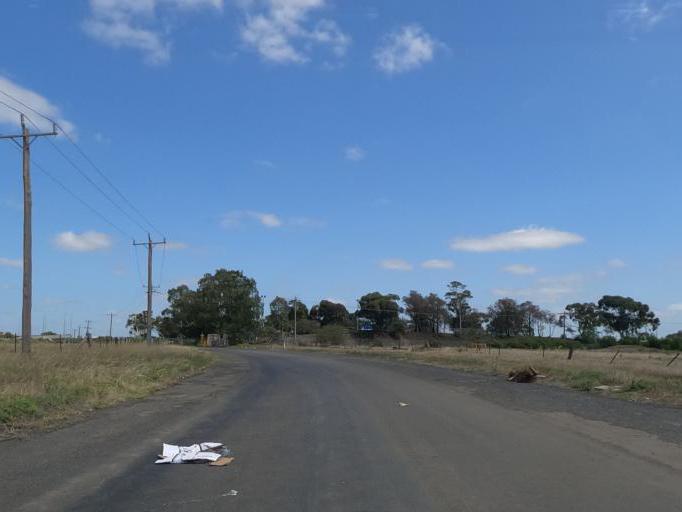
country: AU
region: Victoria
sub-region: Hume
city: Westmeadows
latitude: -37.6769
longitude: 144.8678
